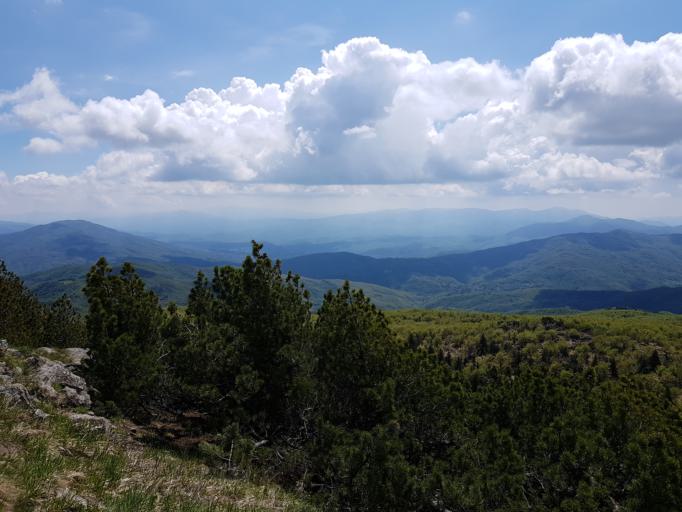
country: IT
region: Liguria
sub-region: Provincia di Genova
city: Santo Stefano d'Aveto
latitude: 44.5618
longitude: 9.5086
